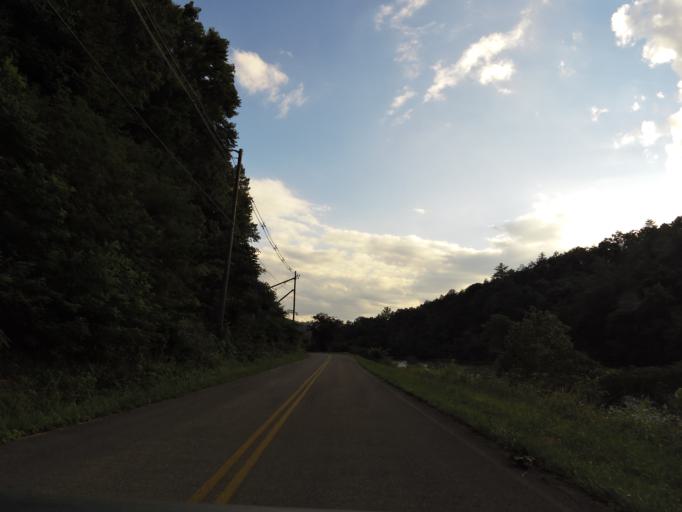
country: US
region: Tennessee
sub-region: Loudon County
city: Greenback
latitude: 35.5605
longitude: -84.0067
